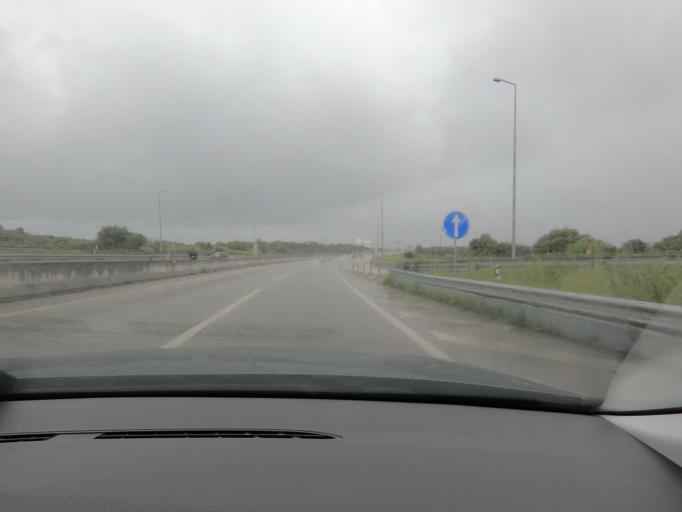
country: PT
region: Lisbon
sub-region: Sintra
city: Sintra
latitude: 38.8127
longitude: -9.3576
